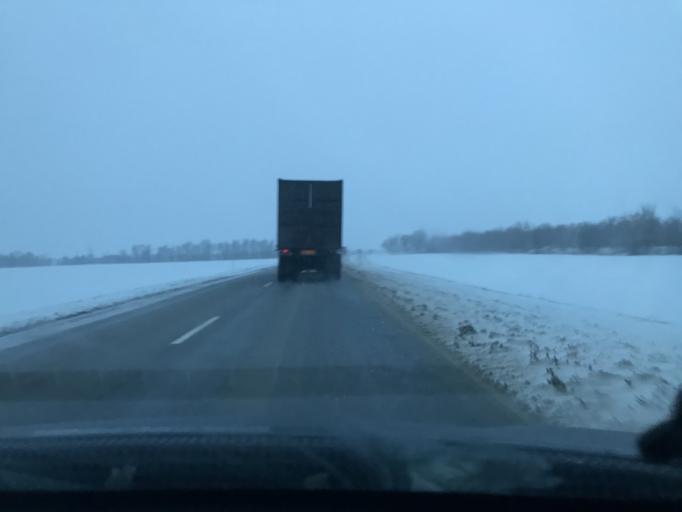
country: RU
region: Rostov
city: Letnik
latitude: 46.0630
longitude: 41.2066
